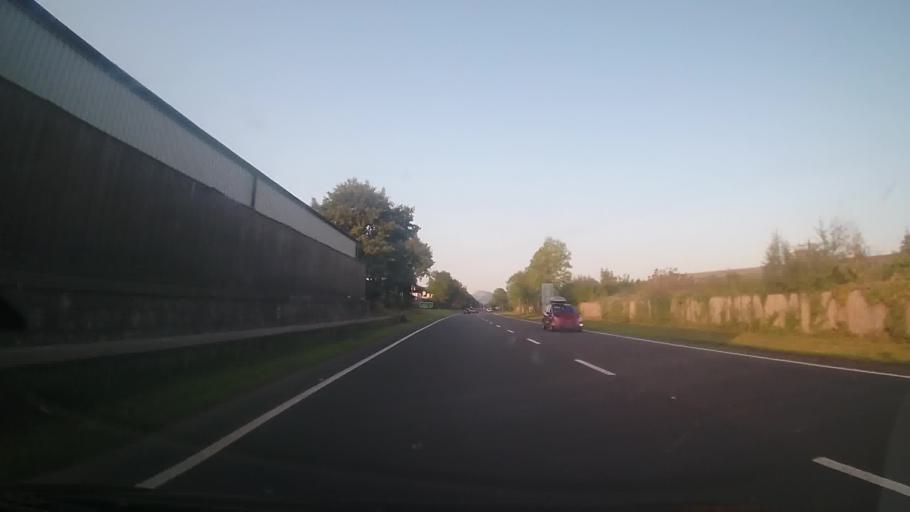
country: GB
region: Wales
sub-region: Sir Powys
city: Welshpool
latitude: 52.6597
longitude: -3.1377
